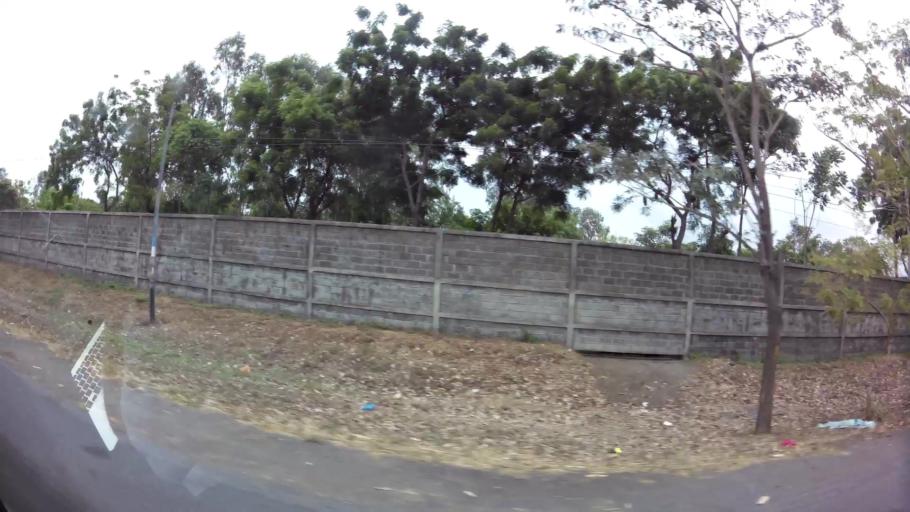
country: NI
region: Leon
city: Quezalguaque
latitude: 12.5326
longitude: -86.8949
